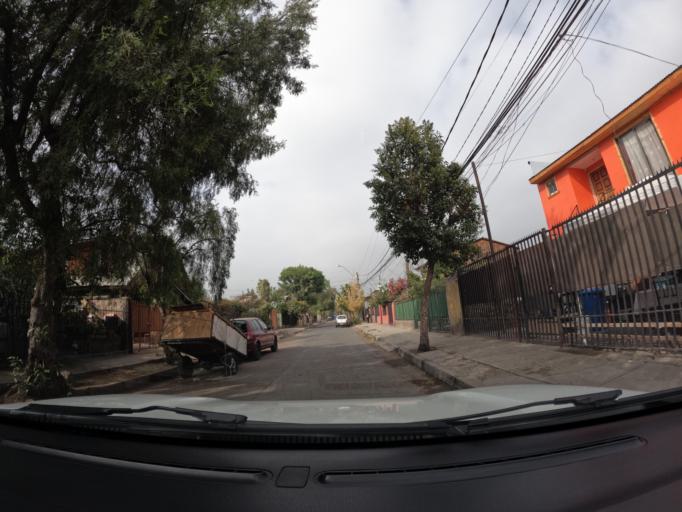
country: CL
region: Santiago Metropolitan
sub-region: Provincia de Santiago
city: Villa Presidente Frei, Nunoa, Santiago, Chile
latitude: -33.4729
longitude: -70.5481
